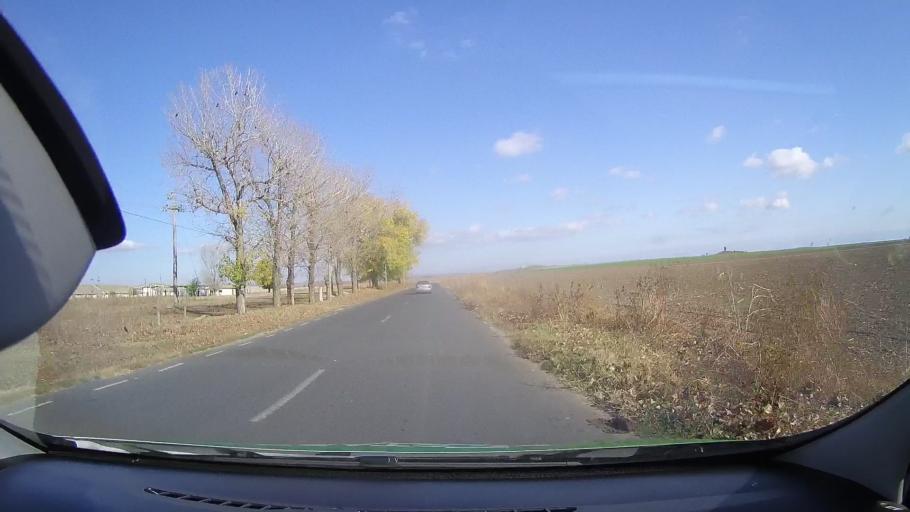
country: RO
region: Tulcea
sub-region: Comuna Baia
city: Baia
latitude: 44.7350
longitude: 28.6867
